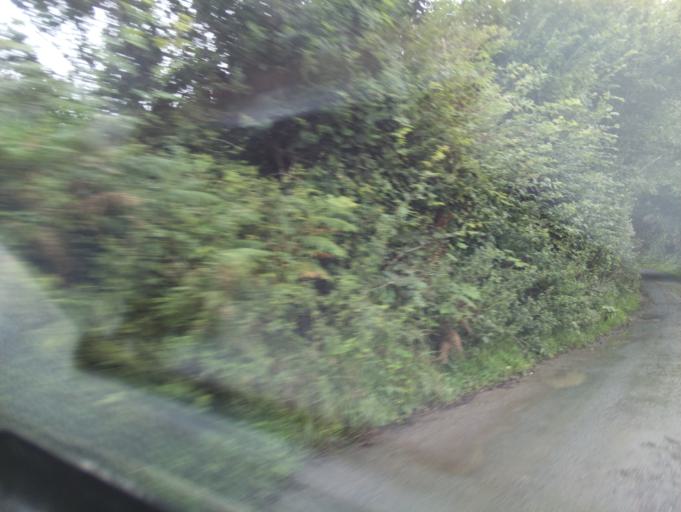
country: GB
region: England
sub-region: Devon
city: Dartmouth
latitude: 50.3472
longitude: -3.6399
